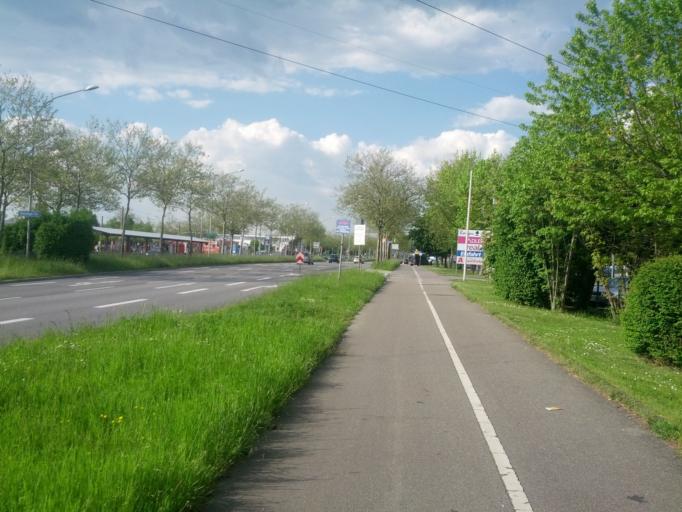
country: DE
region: Baden-Wuerttemberg
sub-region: Freiburg Region
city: Ebringen
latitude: 47.9873
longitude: 7.7967
